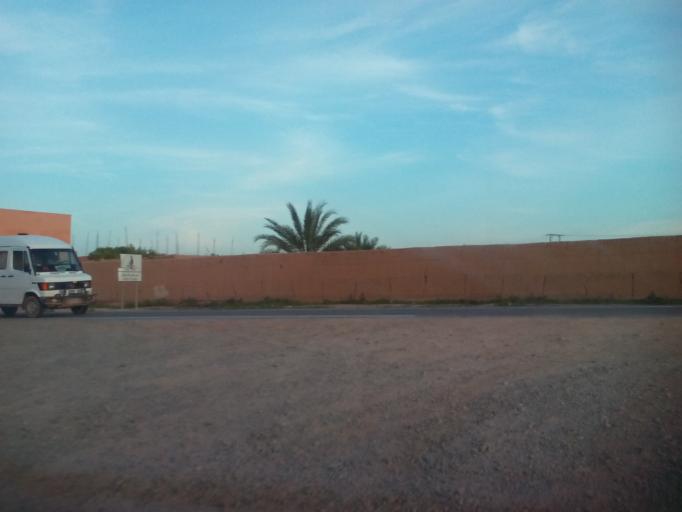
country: MA
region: Marrakech-Tensift-Al Haouz
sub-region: Marrakech
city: Marrakesh
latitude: 31.6251
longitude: -8.2834
